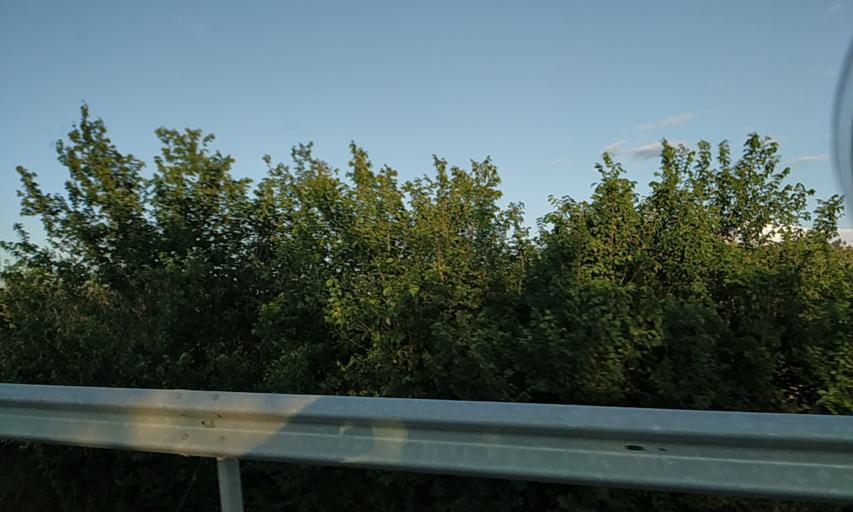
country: ES
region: Extremadura
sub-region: Provincia de Caceres
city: Valencia de Alcantara
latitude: 39.4156
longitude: -7.2285
